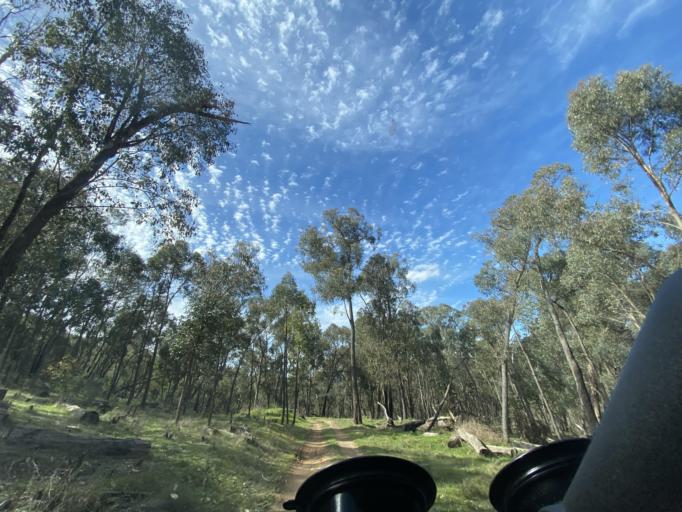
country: AU
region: Victoria
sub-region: Mansfield
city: Mansfield
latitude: -36.8084
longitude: 146.1192
